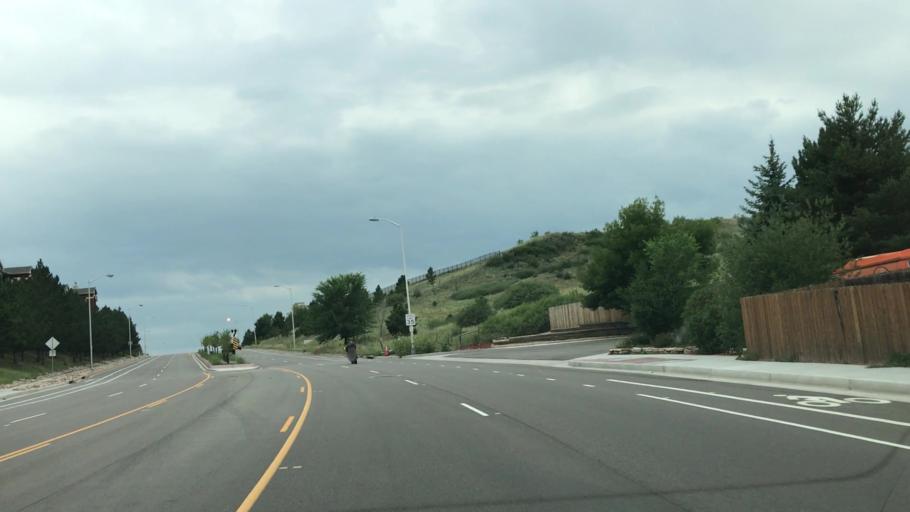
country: US
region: Colorado
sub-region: El Paso County
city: Colorado Springs
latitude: 38.8849
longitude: -104.8477
